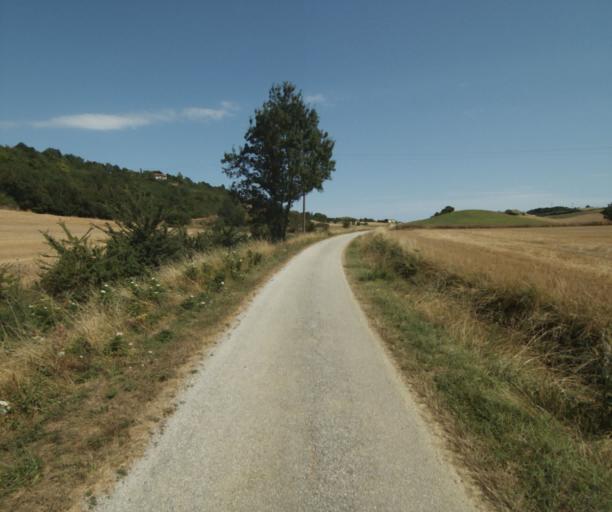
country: FR
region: Midi-Pyrenees
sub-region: Departement de la Haute-Garonne
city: Saint-Felix-Lauragais
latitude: 43.4514
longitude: 1.8742
